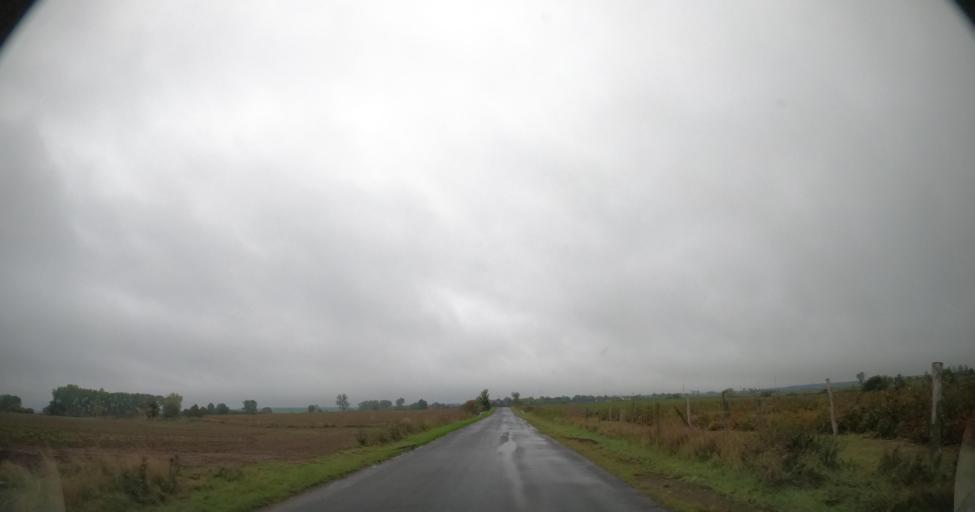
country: PL
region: West Pomeranian Voivodeship
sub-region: Powiat pyrzycki
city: Kozielice
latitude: 53.0555
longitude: 14.7781
